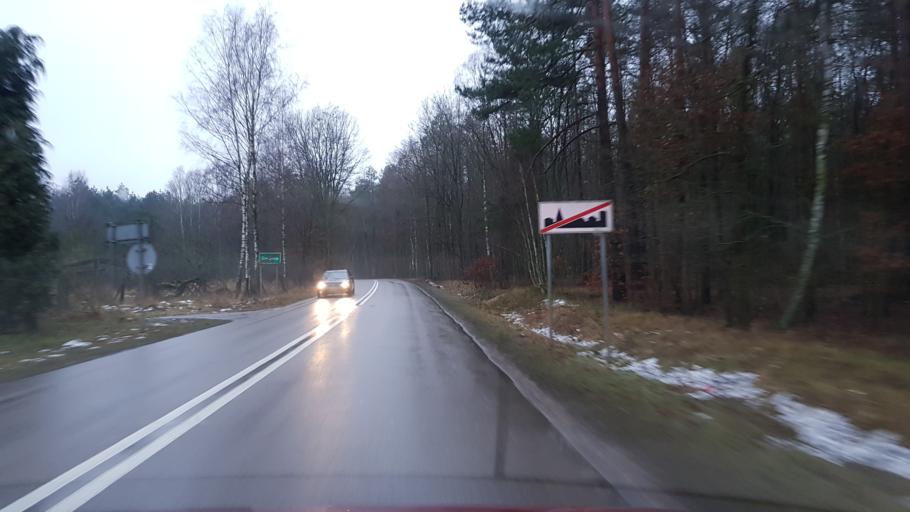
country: PL
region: West Pomeranian Voivodeship
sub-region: Powiat policki
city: Police
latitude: 53.5255
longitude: 14.5275
